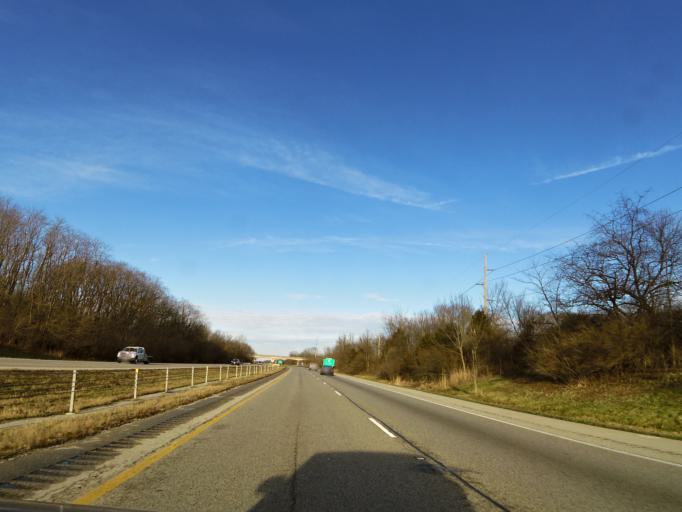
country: US
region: Illinois
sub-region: Vermilion County
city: Catlin
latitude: 40.1176
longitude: -87.6980
